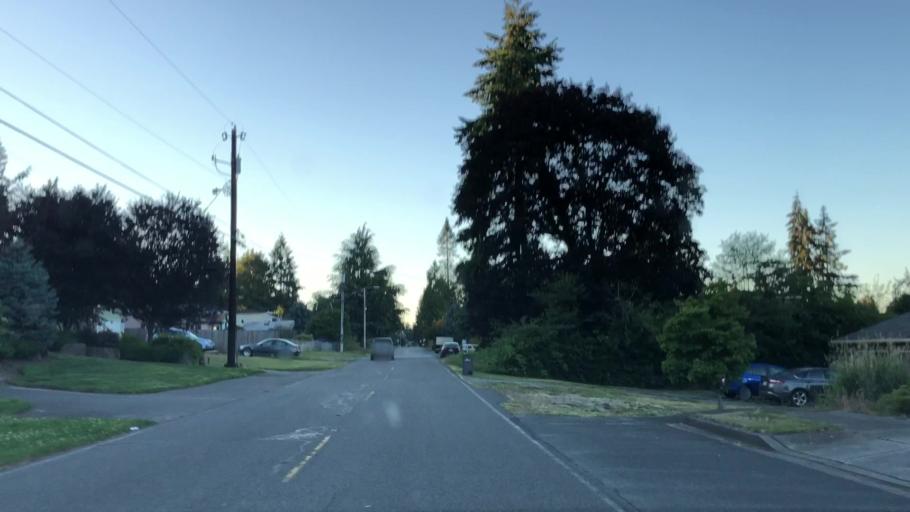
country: US
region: Washington
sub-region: Snohomish County
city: Brier
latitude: 47.7856
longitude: -122.2720
